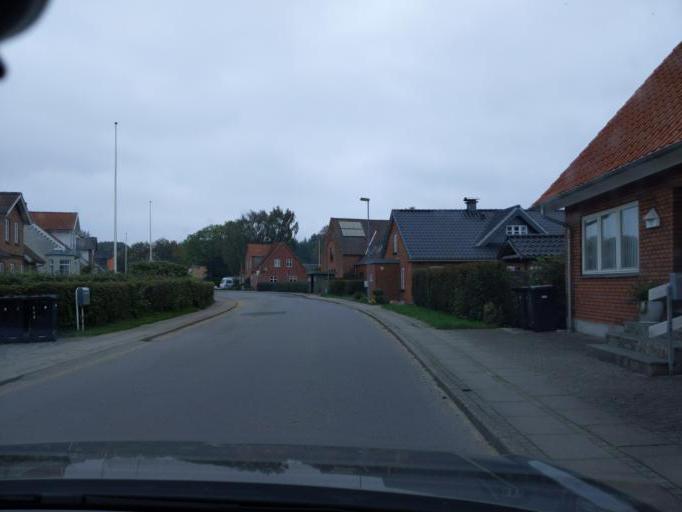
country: DK
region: Central Jutland
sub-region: Viborg Kommune
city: Stoholm
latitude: 56.4772
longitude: 9.2290
